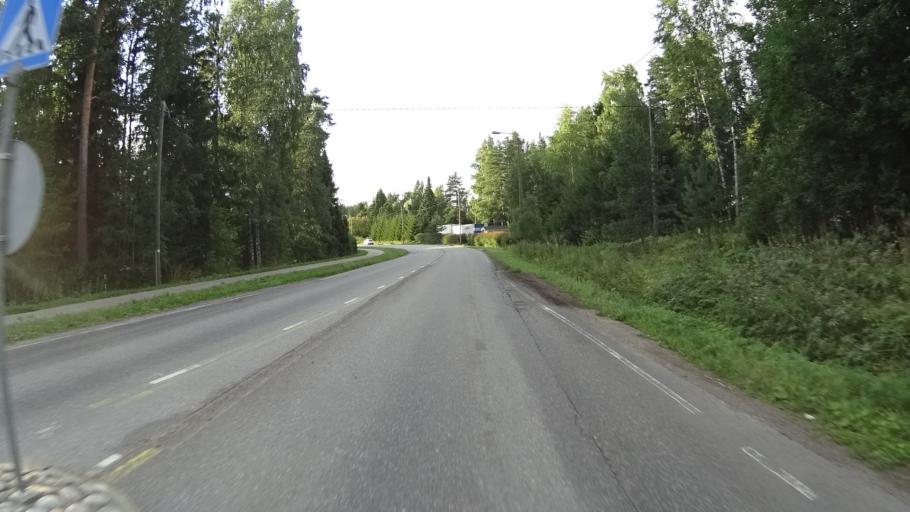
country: FI
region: Uusimaa
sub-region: Helsinki
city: Kilo
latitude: 60.3277
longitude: 24.8656
